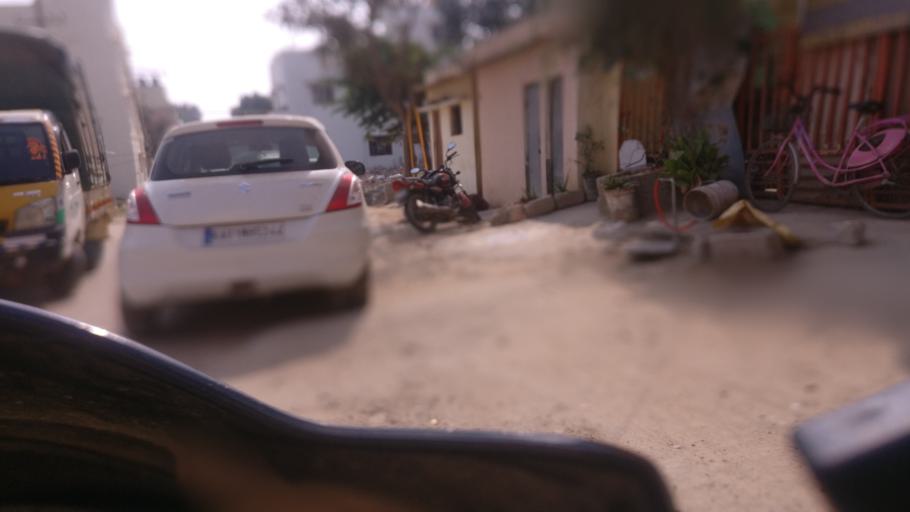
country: IN
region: Karnataka
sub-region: Bangalore Urban
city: Bangalore
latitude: 12.8964
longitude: 77.6803
